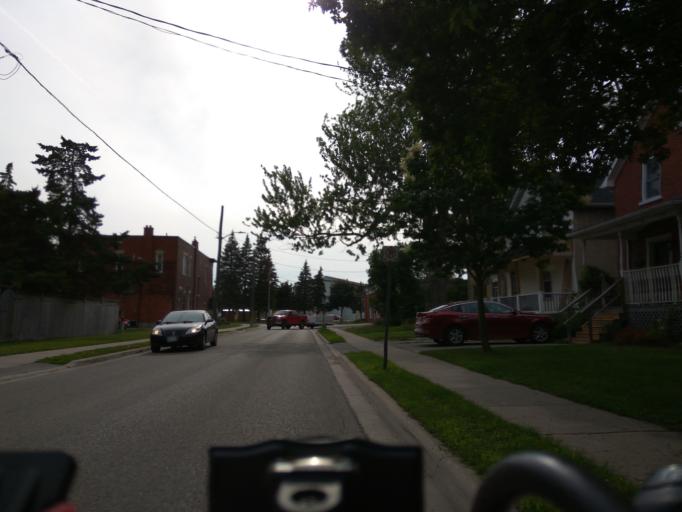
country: CA
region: Ontario
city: Stratford
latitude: 43.3657
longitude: -80.9783
